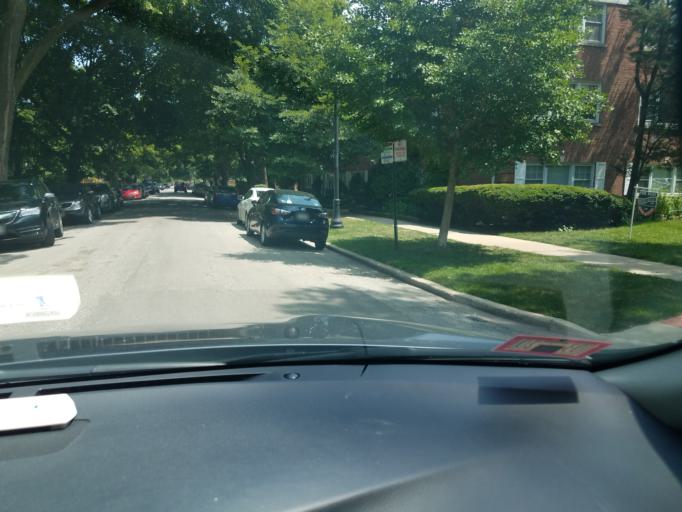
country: US
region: Illinois
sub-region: Cook County
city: Evanston
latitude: 42.0394
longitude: -87.6865
